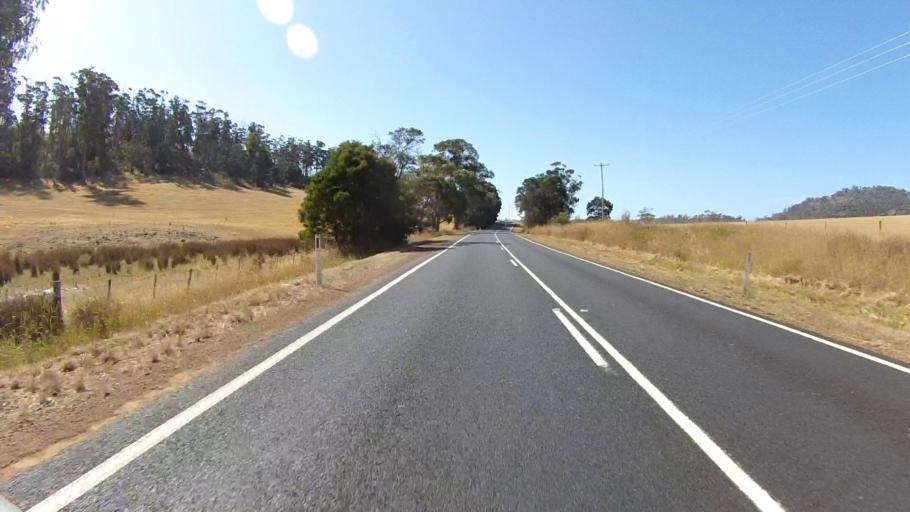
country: AU
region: Tasmania
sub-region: Sorell
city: Sorell
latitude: -42.4266
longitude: 147.9327
